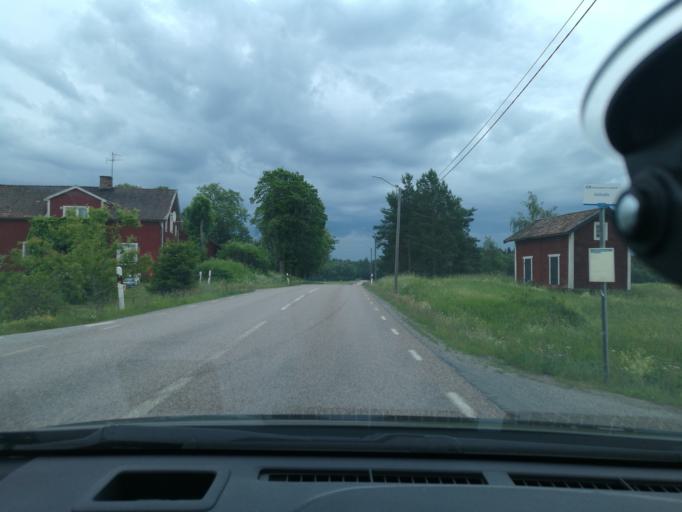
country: SE
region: Vaestmanland
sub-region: Sala Kommun
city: Sala
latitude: 59.9156
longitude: 16.4370
